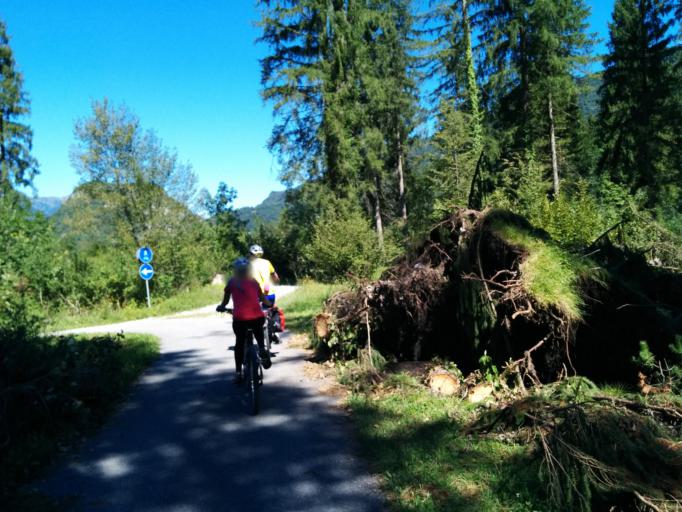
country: IT
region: Friuli Venezia Giulia
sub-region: Provincia di Udine
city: Villa Santina
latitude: 46.4140
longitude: 12.9102
